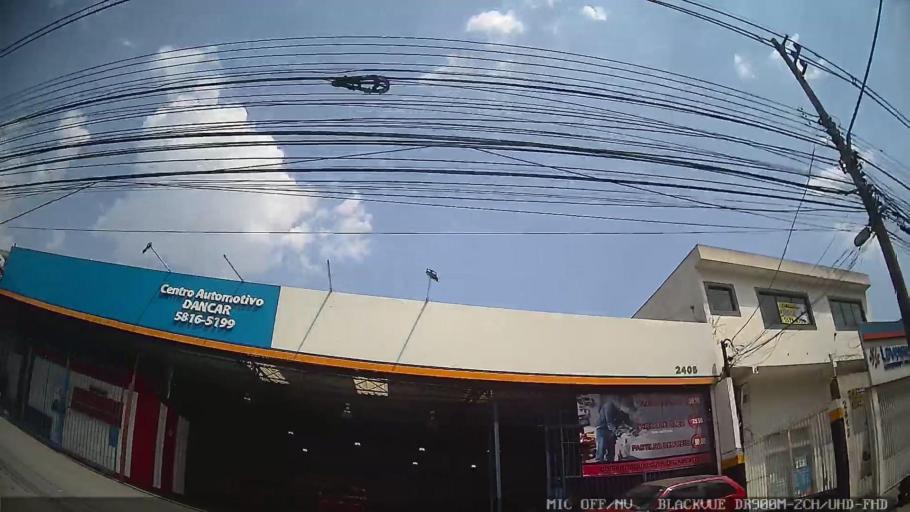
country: BR
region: Sao Paulo
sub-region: Taboao Da Serra
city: Taboao da Serra
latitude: -23.6502
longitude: -46.7561
